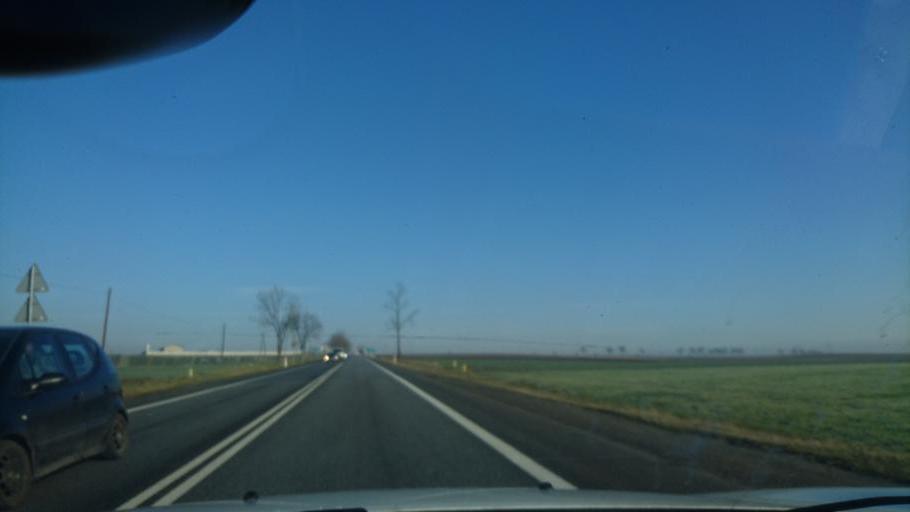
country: PL
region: Opole Voivodeship
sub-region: Powiat nyski
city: Pakoslawice
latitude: 50.5450
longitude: 17.3716
